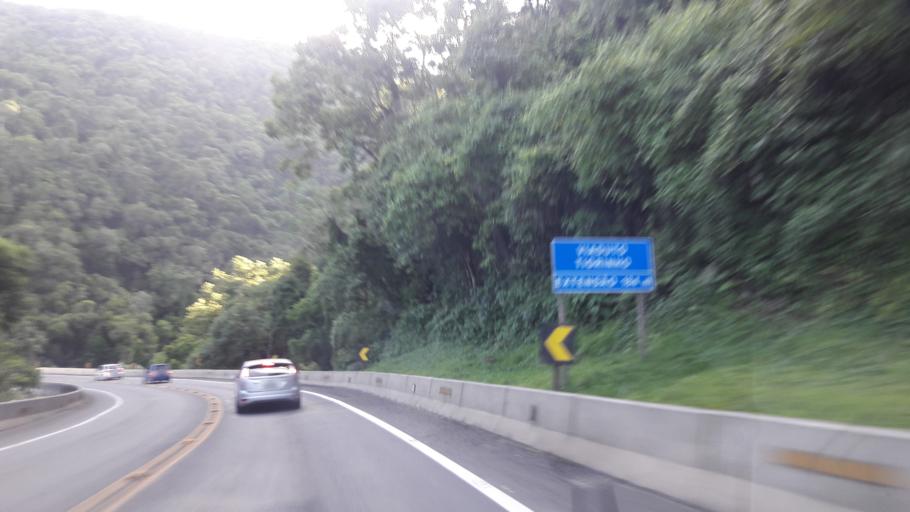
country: BR
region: Parana
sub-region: Prudentopolis
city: Prudentopolis
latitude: -25.3216
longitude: -51.1964
